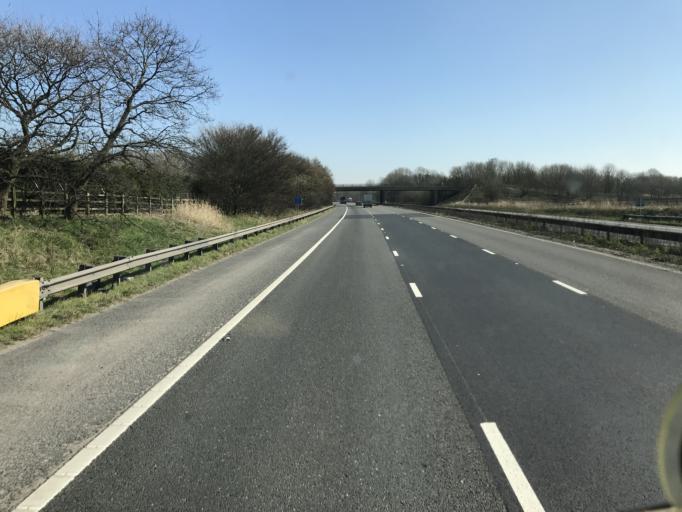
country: GB
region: England
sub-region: Borough of Halton
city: Daresbury
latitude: 53.3289
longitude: -2.6249
